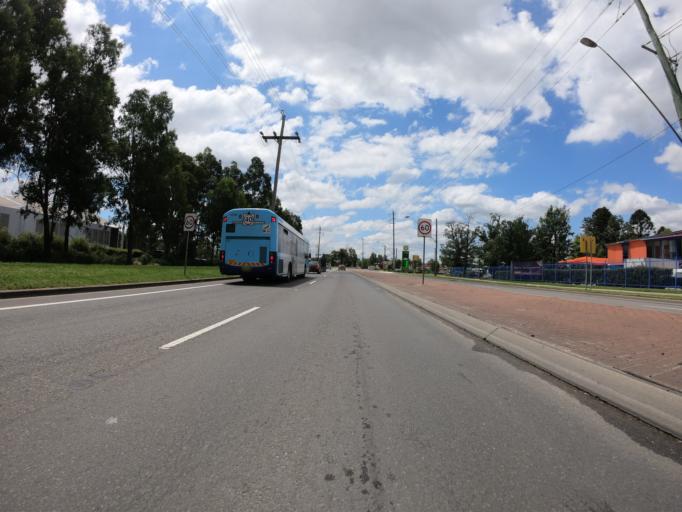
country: AU
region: New South Wales
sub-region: Penrith Municipality
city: Penrith
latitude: -33.7444
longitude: 150.6914
